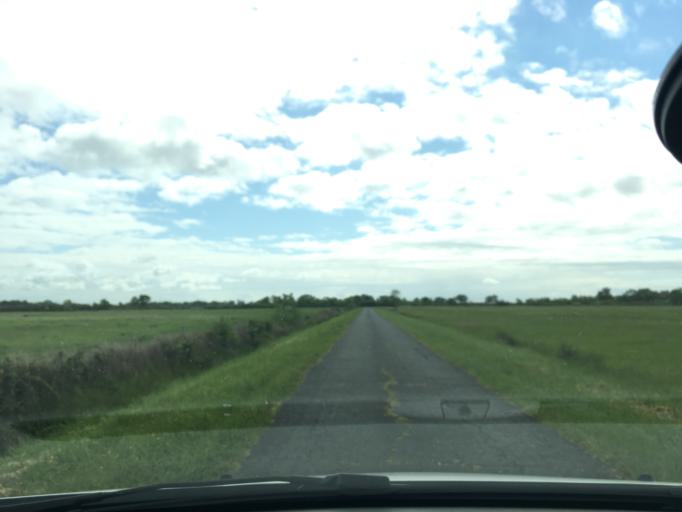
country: FR
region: Aquitaine
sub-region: Departement de la Gironde
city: Saint-Estephe
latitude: 45.3317
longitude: -0.8068
